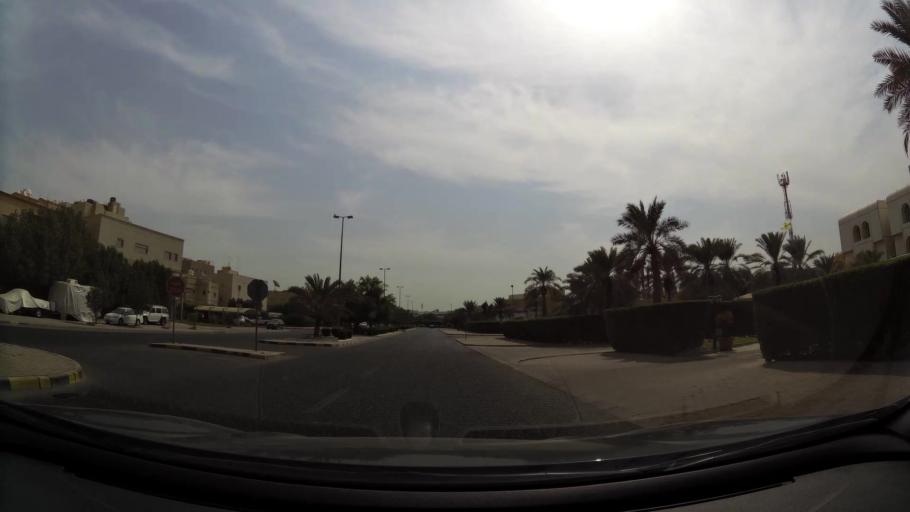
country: KW
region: Al Asimah
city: Ash Shamiyah
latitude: 29.3356
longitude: 47.9815
